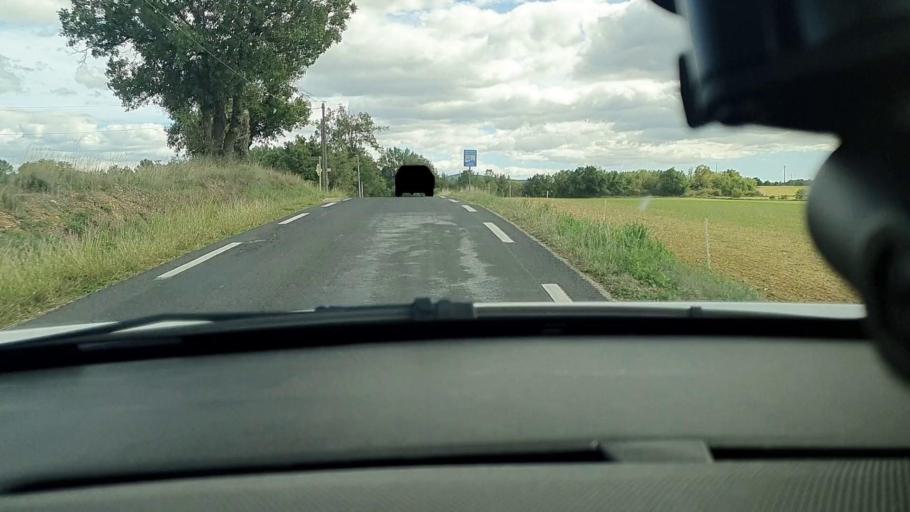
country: FR
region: Languedoc-Roussillon
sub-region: Departement du Gard
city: Les Mages
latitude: 44.1958
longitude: 4.2130
